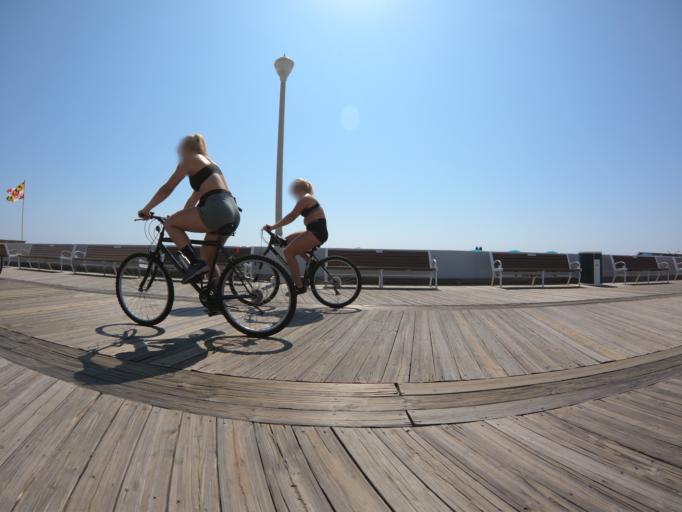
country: US
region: Maryland
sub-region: Worcester County
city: Ocean City
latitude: 38.3408
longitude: -75.0799
